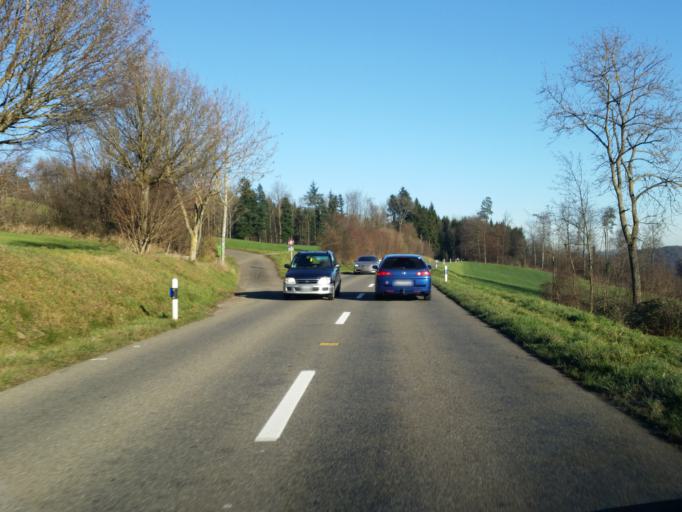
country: CH
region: Aargau
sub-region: Bezirk Bremgarten
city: Rudolfstetten
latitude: 47.3733
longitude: 8.3732
